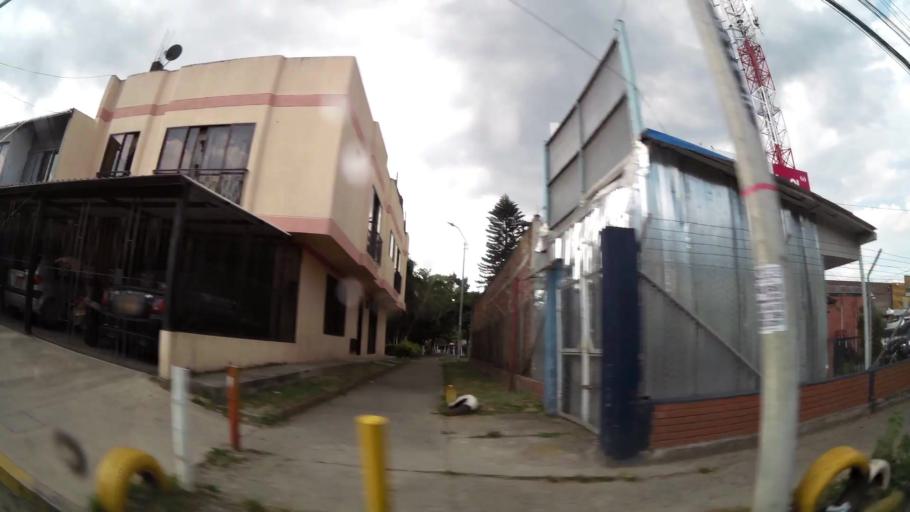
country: CO
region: Valle del Cauca
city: Cali
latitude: 3.4661
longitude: -76.4900
